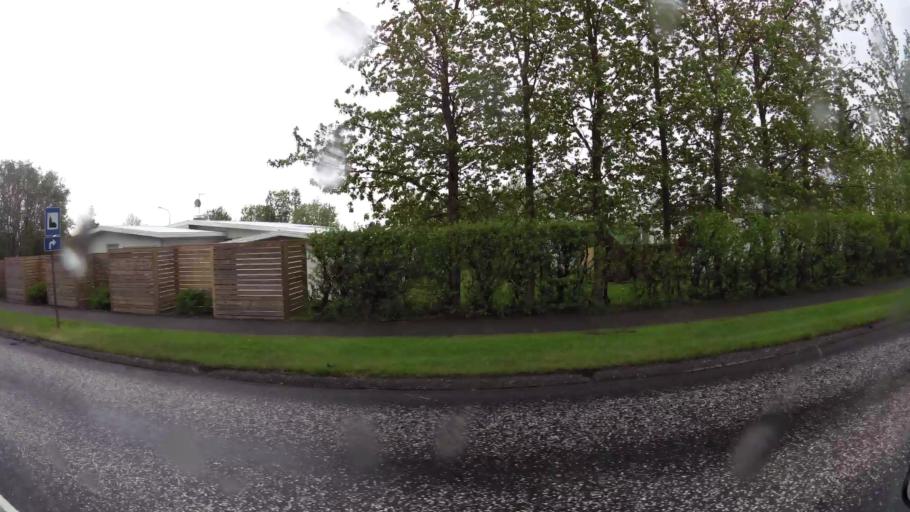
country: IS
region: Capital Region
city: Gardabaer
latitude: 64.0873
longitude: -21.9084
